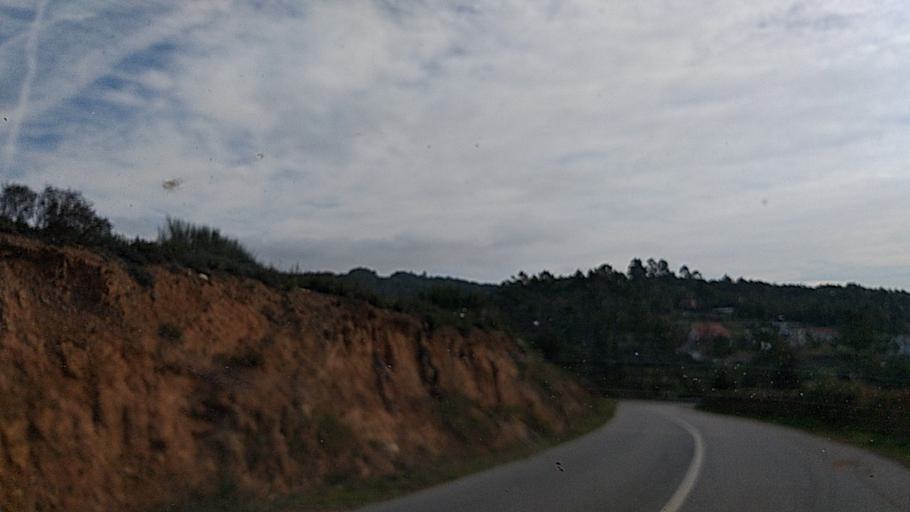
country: PT
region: Guarda
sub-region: Fornos de Algodres
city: Fornos de Algodres
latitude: 40.6842
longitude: -7.5350
